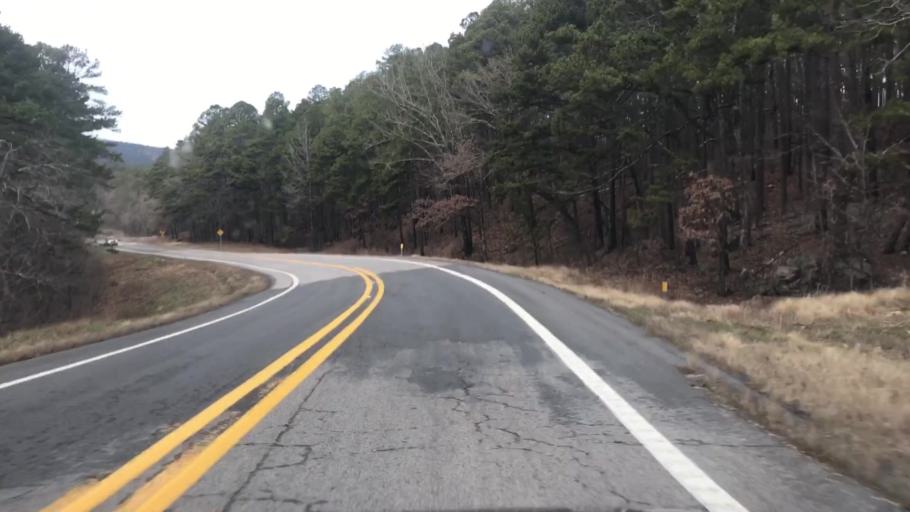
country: US
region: Arkansas
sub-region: Montgomery County
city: Mount Ida
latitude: 34.6842
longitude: -93.8021
